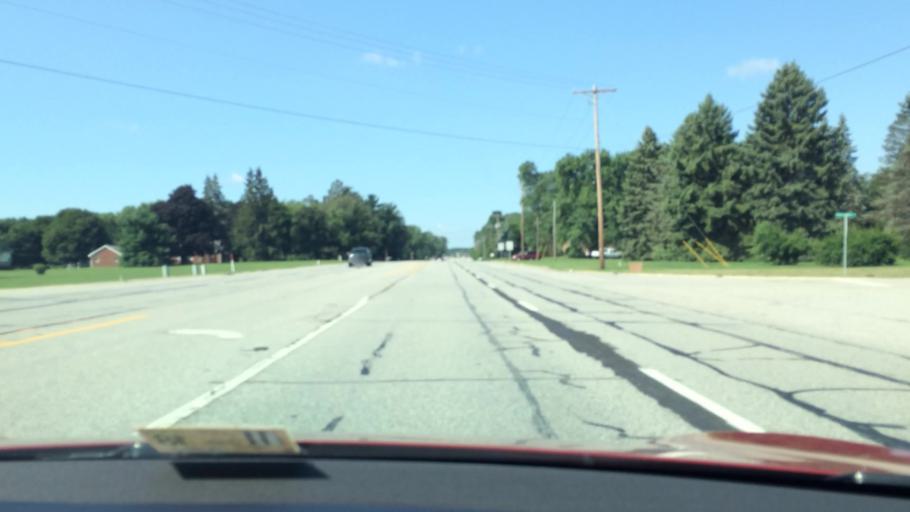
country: US
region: Indiana
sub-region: Saint Joseph County
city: Granger
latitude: 41.7317
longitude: -86.1615
